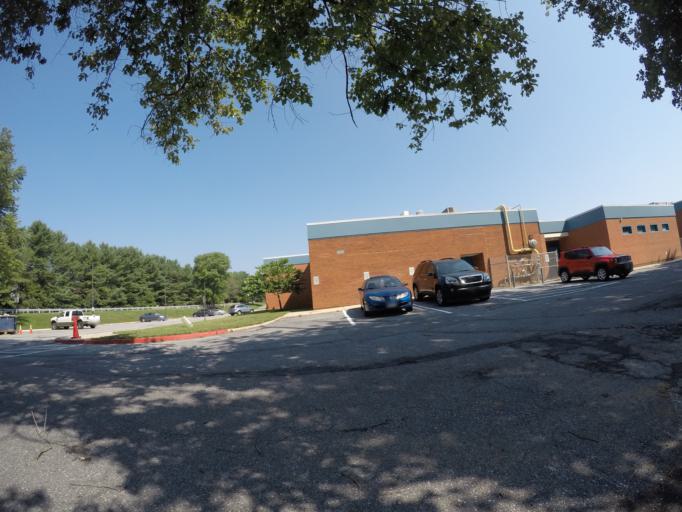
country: US
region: Maryland
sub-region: Howard County
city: Columbia
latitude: 39.2656
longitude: -76.8616
